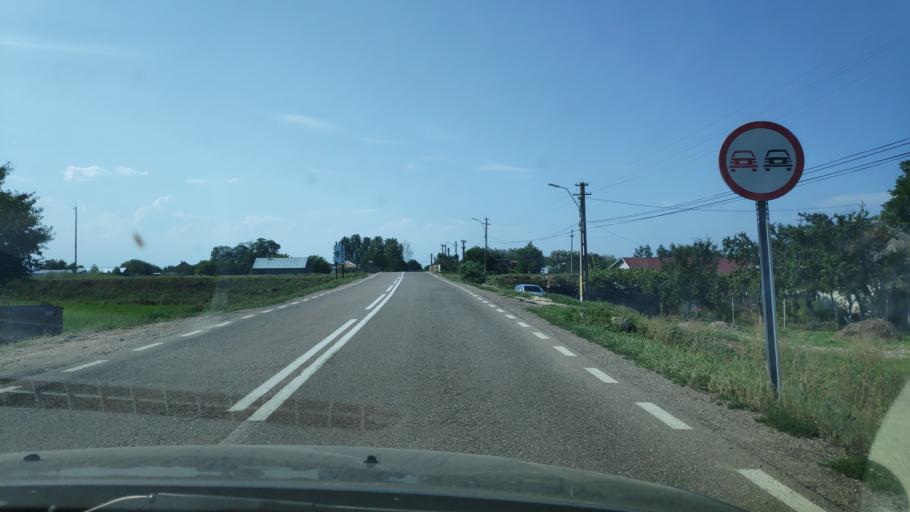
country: RO
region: Suceava
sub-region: Comuna Boroaia
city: Boroaia
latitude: 47.3783
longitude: 26.3201
